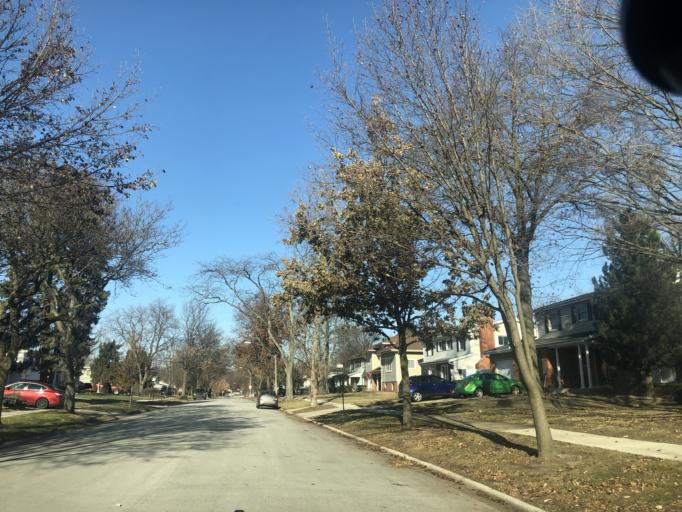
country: US
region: Illinois
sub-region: DuPage County
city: Addison
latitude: 41.9312
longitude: -88.0089
